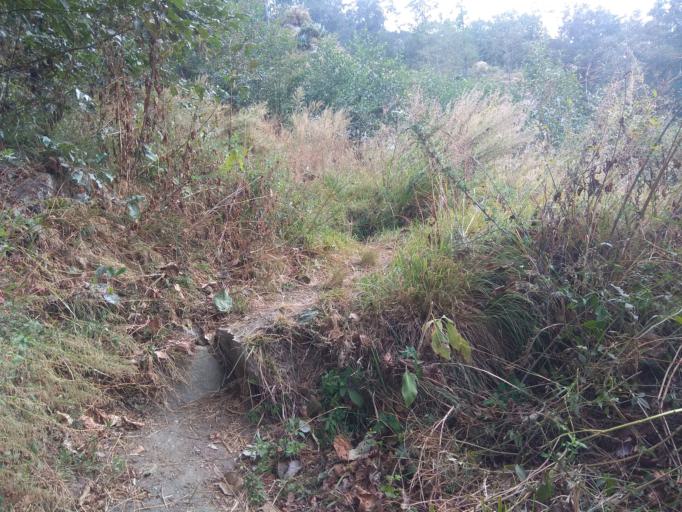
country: NP
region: Far Western
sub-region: Seti Zone
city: Achham
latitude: 29.2321
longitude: 81.6445
